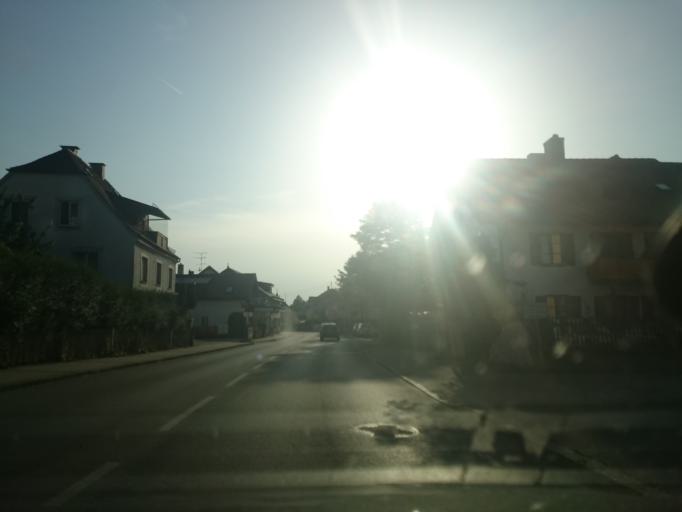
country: DE
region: Bavaria
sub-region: Upper Bavaria
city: Herrsching am Ammersee
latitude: 47.9991
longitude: 11.1805
